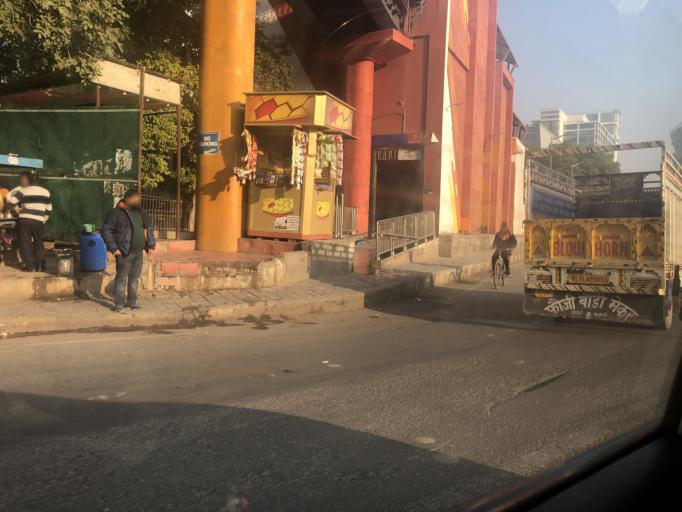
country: IN
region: Haryana
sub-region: Gurgaon
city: Gurgaon
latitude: 28.4981
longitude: 77.0896
